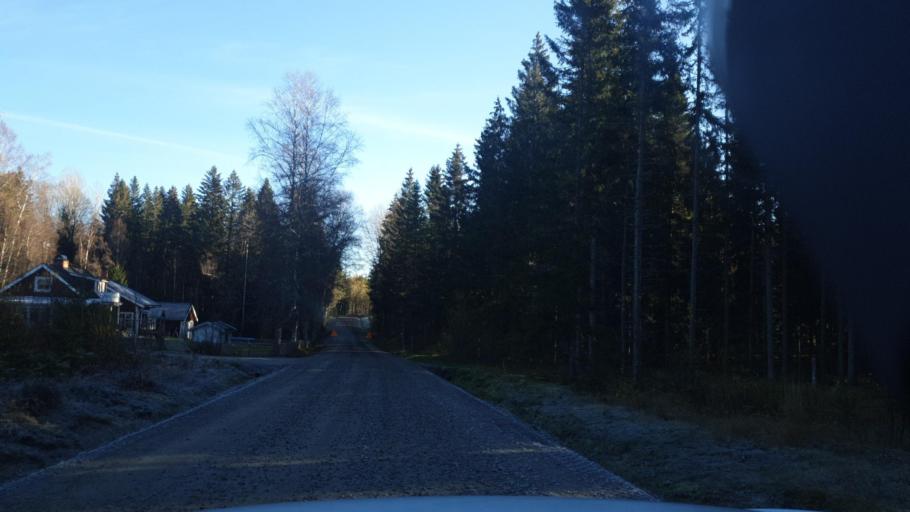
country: SE
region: Vaermland
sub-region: Karlstads Kommun
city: Valberg
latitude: 59.4163
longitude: 13.1346
